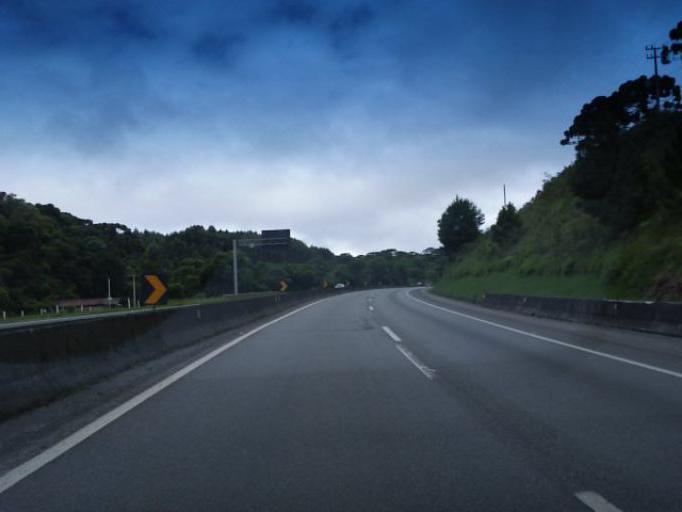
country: BR
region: Parana
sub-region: Campina Grande Do Sul
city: Campina Grande do Sul
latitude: -25.3103
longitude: -49.0088
